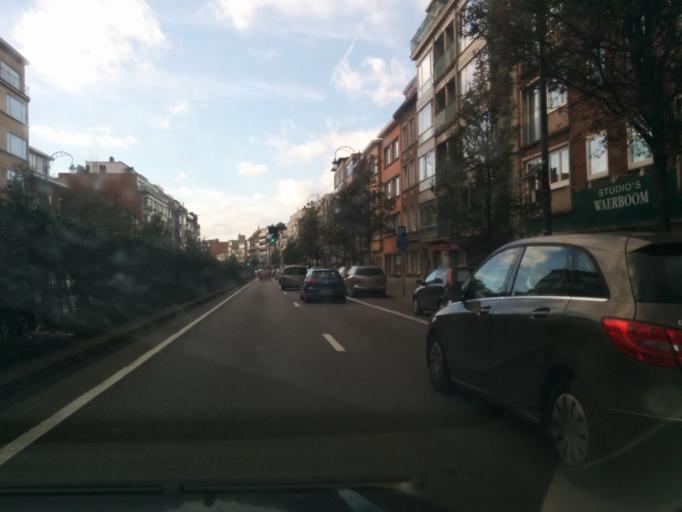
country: BE
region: Flanders
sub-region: Provincie Vlaams-Brabant
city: Wemmel
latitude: 50.8709
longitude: 4.3038
